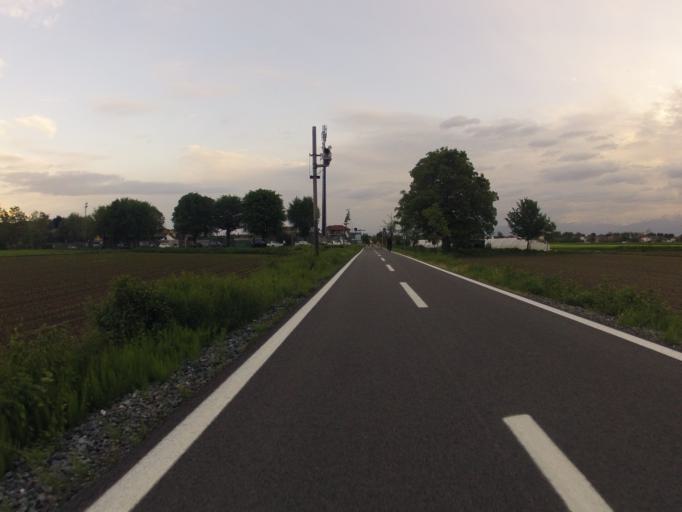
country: IT
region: Piedmont
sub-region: Provincia di Torino
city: Vigone
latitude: 44.8480
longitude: 7.4914
